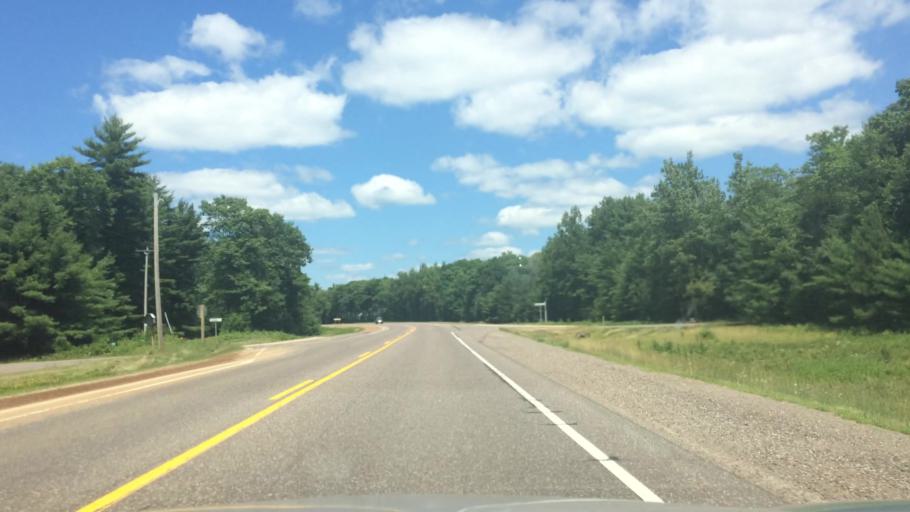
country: US
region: Wisconsin
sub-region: Vilas County
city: Lac du Flambeau
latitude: 45.9392
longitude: -89.6965
